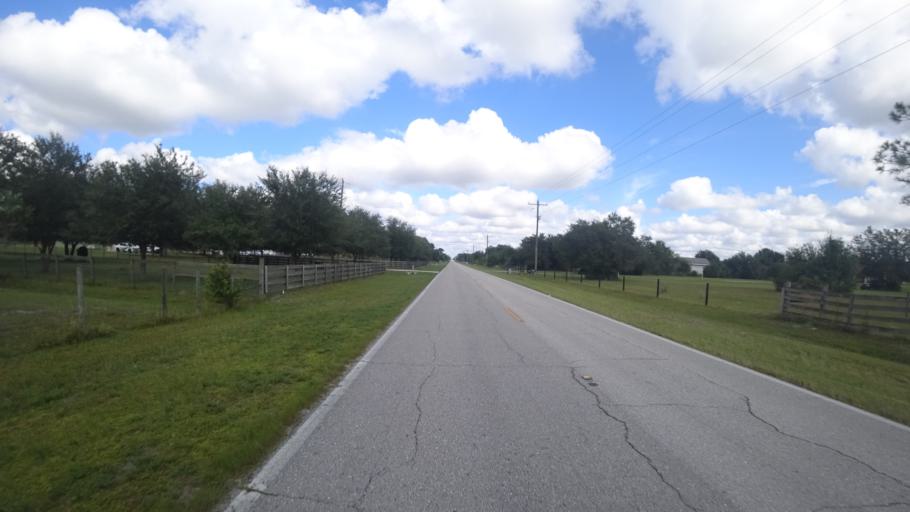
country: US
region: Florida
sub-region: Sarasota County
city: Lake Sarasota
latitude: 27.4021
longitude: -82.2711
